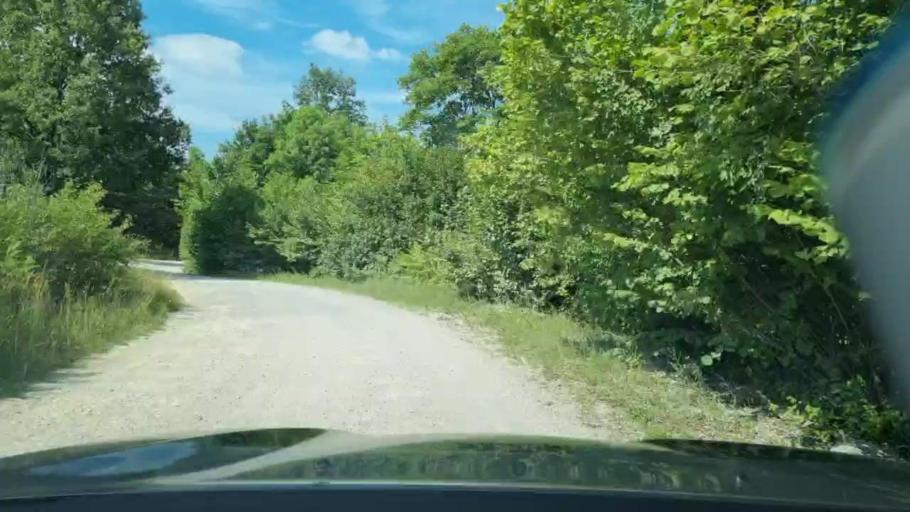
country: BA
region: Federation of Bosnia and Herzegovina
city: Bosanska Krupa
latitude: 44.8235
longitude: 16.1757
